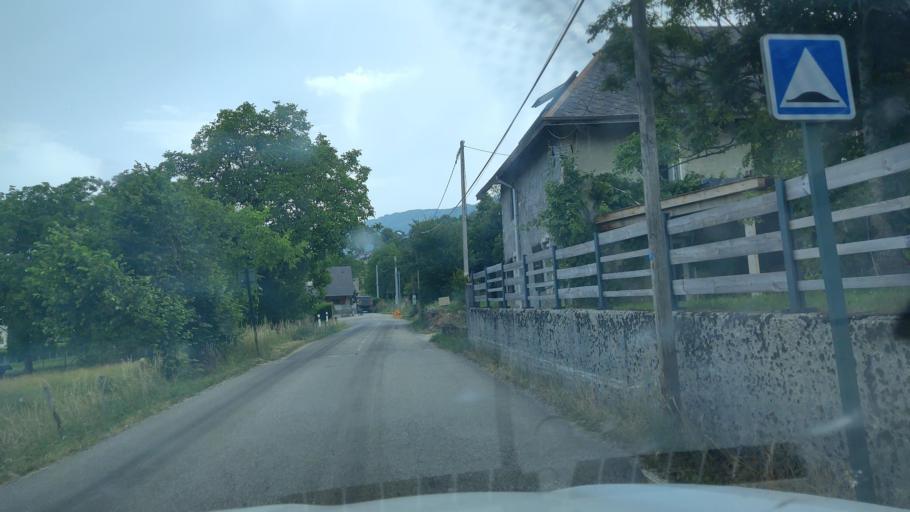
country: FR
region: Rhone-Alpes
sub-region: Departement de la Savoie
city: Barby
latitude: 45.5659
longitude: 6.0242
